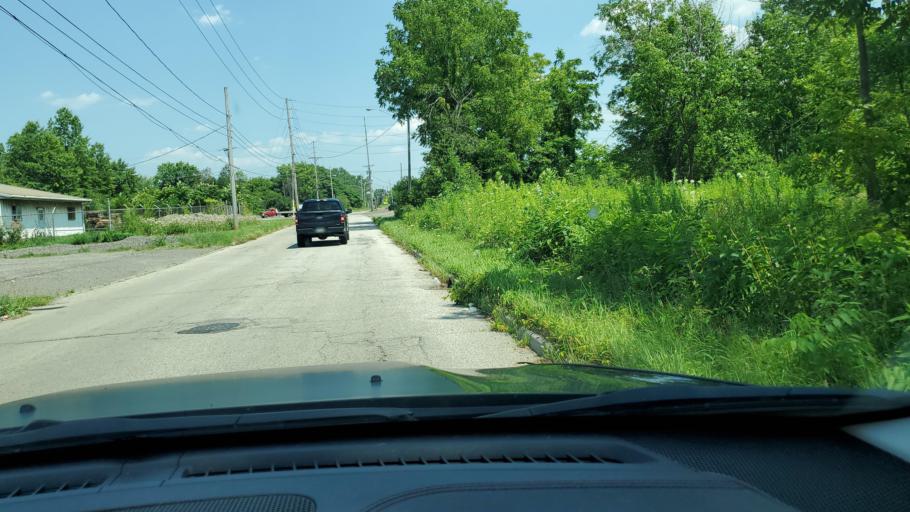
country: US
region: Ohio
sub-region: Trumbull County
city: Warren
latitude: 41.2196
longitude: -80.8032
